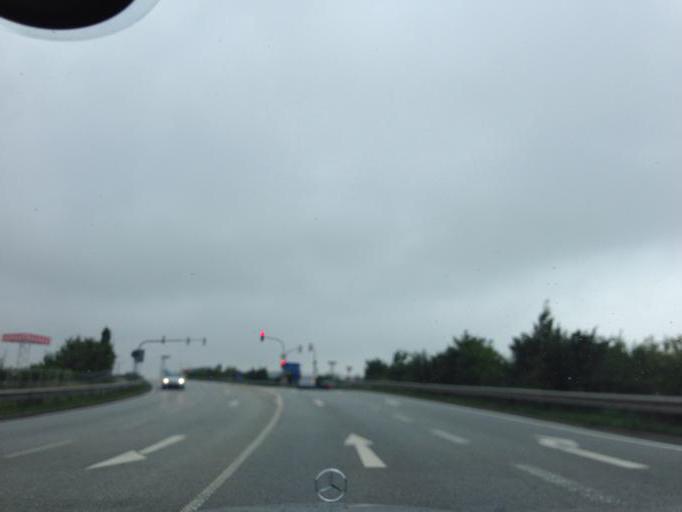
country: DE
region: Schleswig-Holstein
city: Glinde
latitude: 53.5736
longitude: 10.2012
